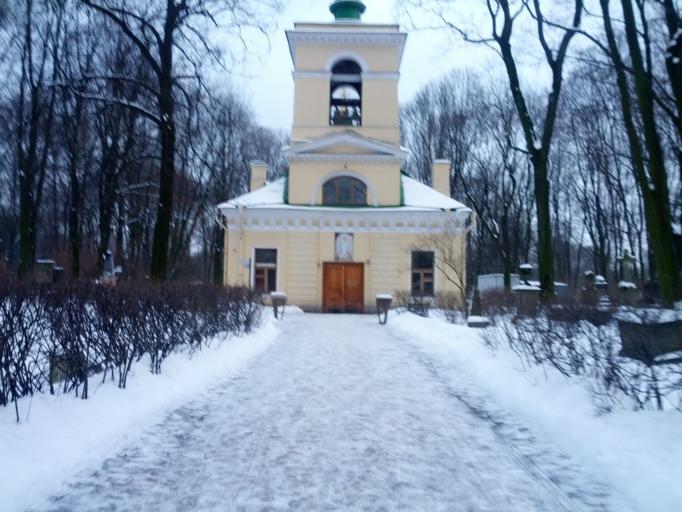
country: RU
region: St.-Petersburg
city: Centralniy
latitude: 59.9044
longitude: 30.3585
